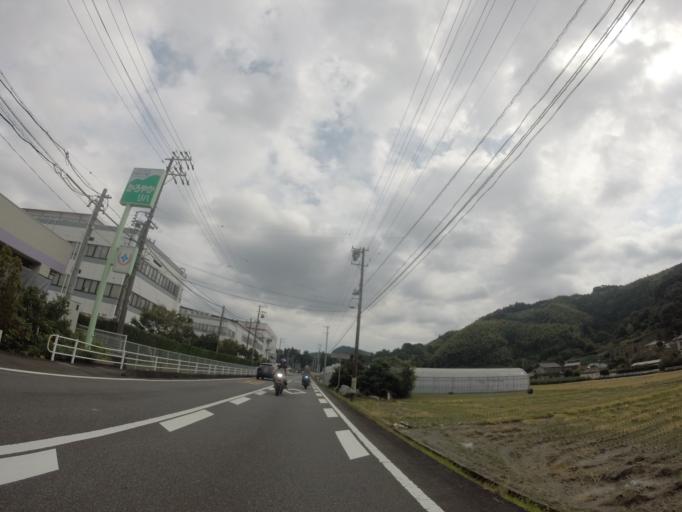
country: JP
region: Shizuoka
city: Fujieda
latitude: 34.8972
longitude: 138.2061
